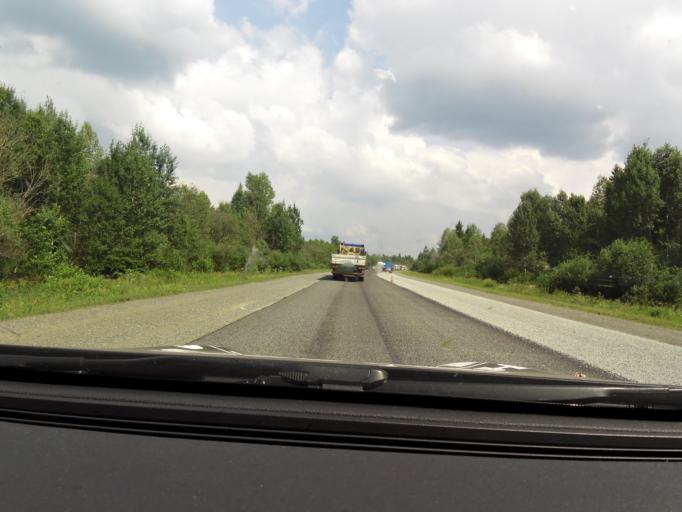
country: RU
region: Sverdlovsk
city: Ufimskiy
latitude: 56.7713
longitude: 58.1063
